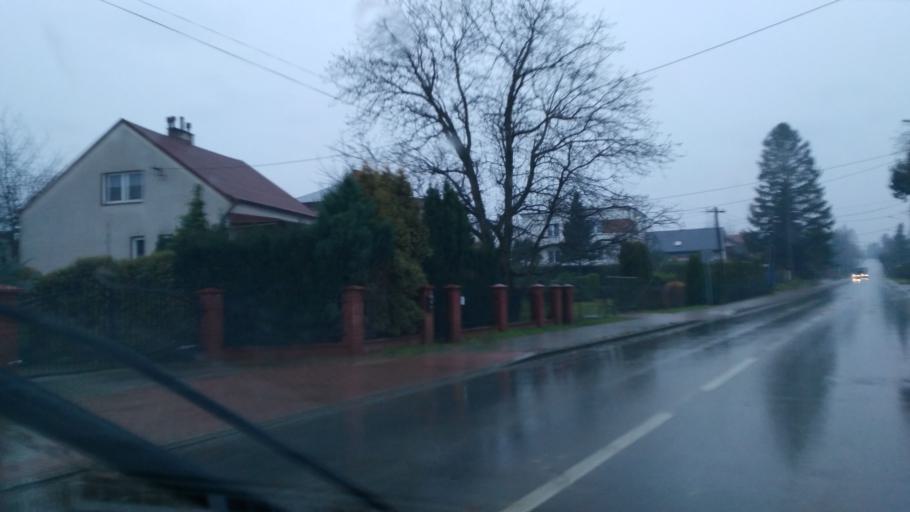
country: PL
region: Subcarpathian Voivodeship
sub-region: Powiat lancucki
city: Lancut
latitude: 50.0707
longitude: 22.2174
